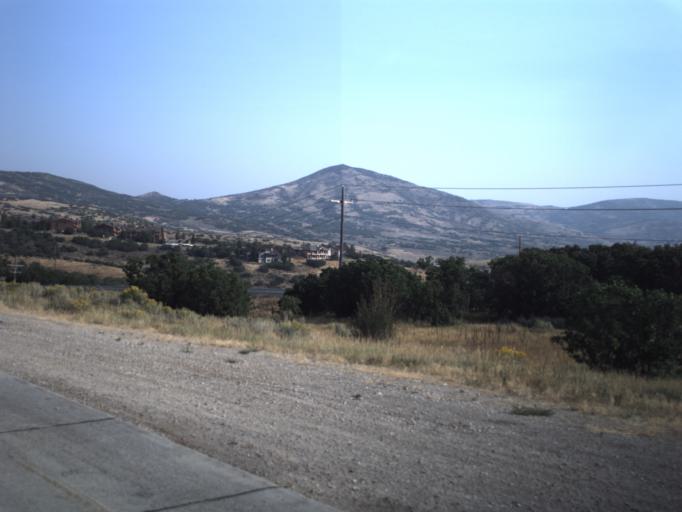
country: US
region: Utah
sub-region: Summit County
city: Park City
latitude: 40.6261
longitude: -111.4400
